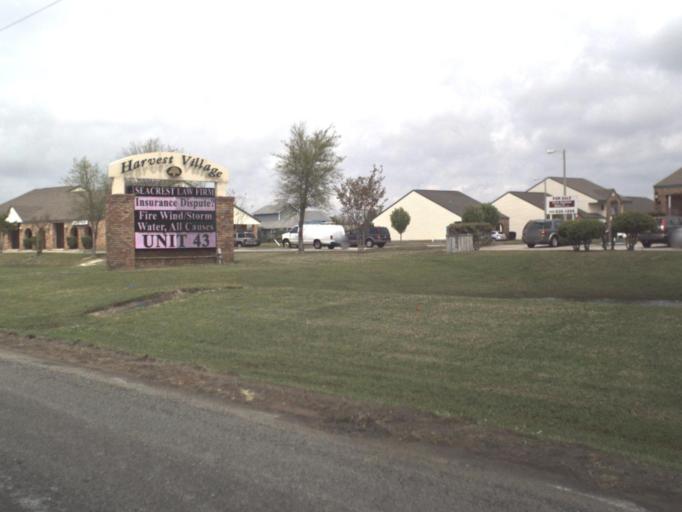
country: US
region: Florida
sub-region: Santa Rosa County
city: Navarre
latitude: 30.4020
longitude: -86.9067
